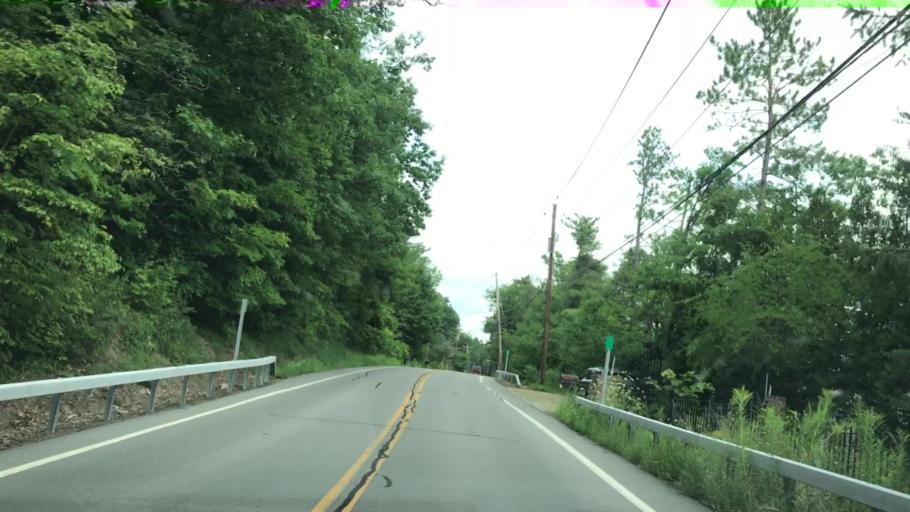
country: US
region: New York
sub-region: Steuben County
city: Sylvan Beach
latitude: 42.5346
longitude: -77.1534
